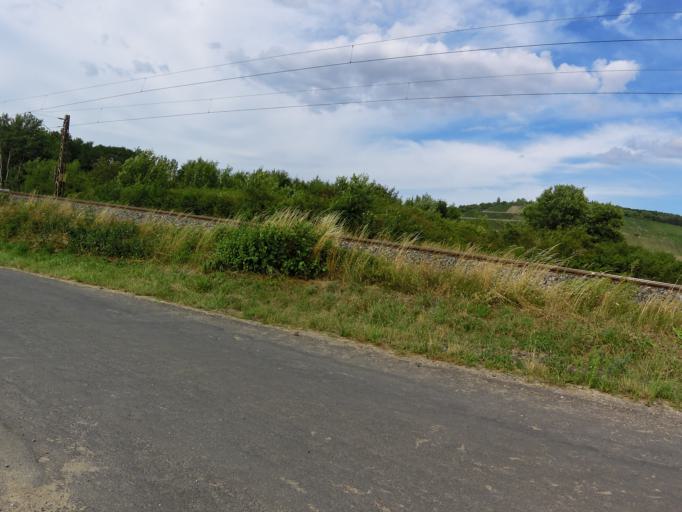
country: DE
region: Bavaria
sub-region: Regierungsbezirk Unterfranken
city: Randersacker
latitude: 49.7457
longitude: 9.9800
